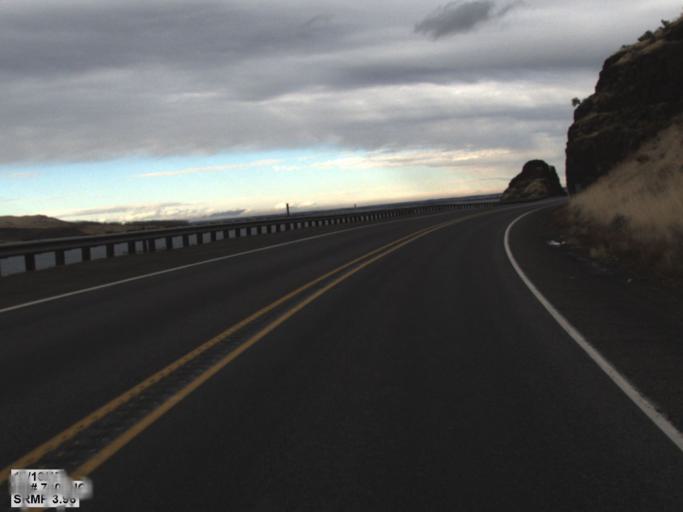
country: US
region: Washington
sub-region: Benton County
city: Finley
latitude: 46.0425
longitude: -118.9405
